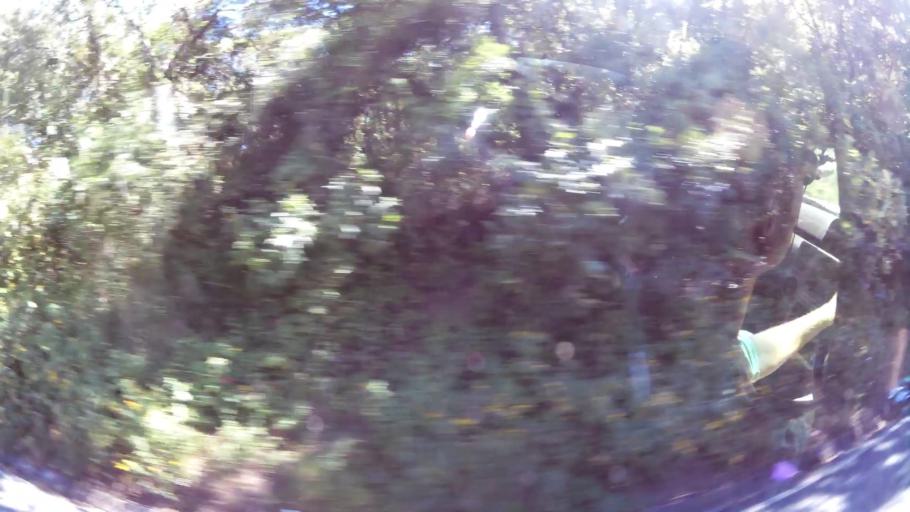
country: GT
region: Solola
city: Solola
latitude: 14.7545
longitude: -91.1770
